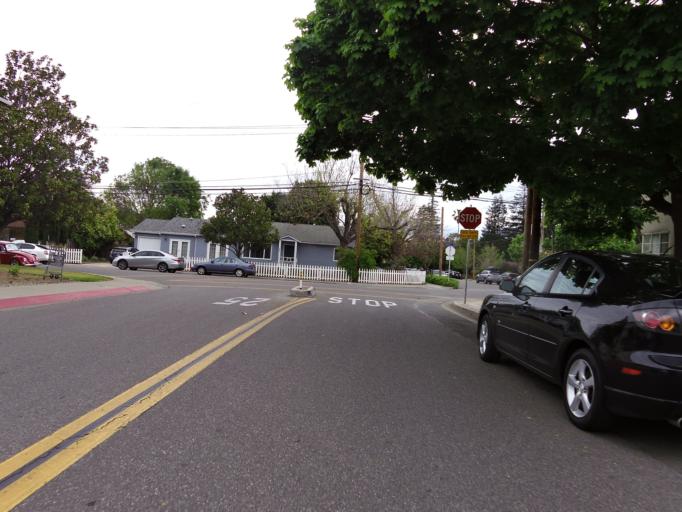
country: US
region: California
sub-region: Santa Clara County
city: Mountain View
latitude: 37.3932
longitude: -122.0927
